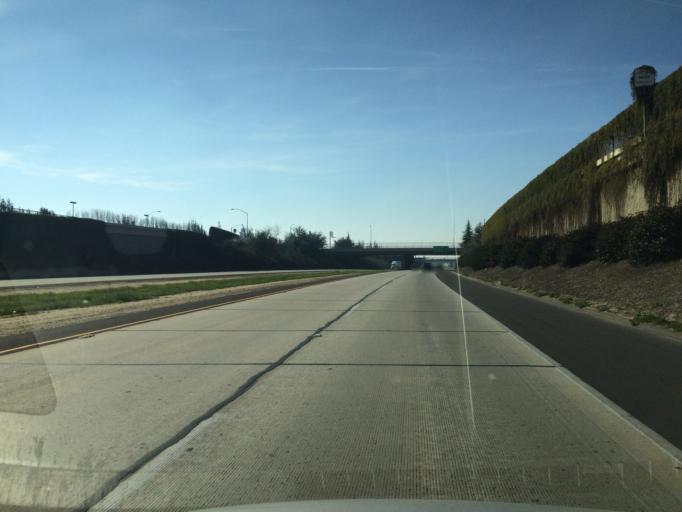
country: US
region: California
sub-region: Tulare County
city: Visalia
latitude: 36.3272
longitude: -119.3288
